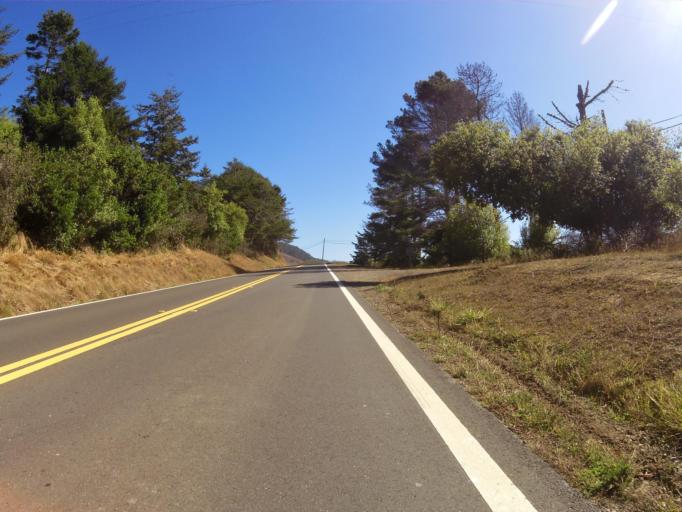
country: US
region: California
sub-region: Mendocino County
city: Fort Bragg
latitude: 39.5900
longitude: -123.7779
